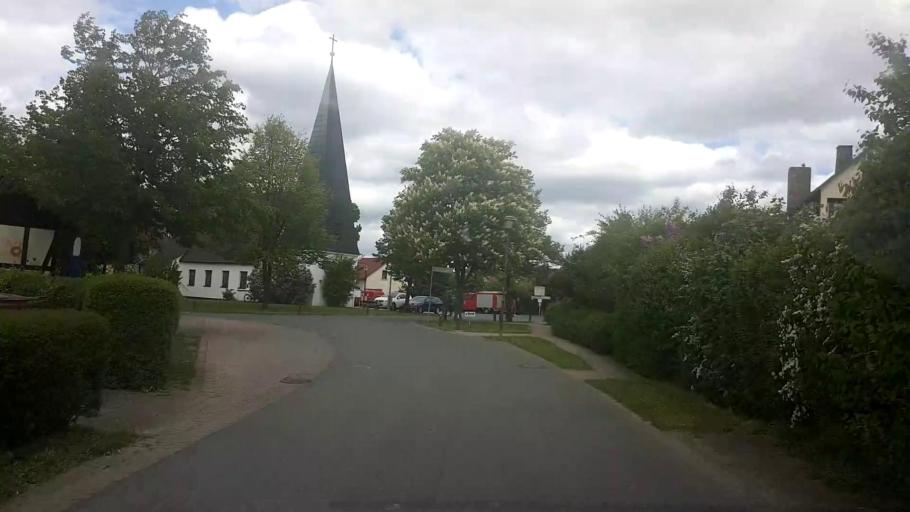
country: DE
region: Bavaria
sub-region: Upper Franconia
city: Lichtenfels
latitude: 50.1314
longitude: 11.0261
